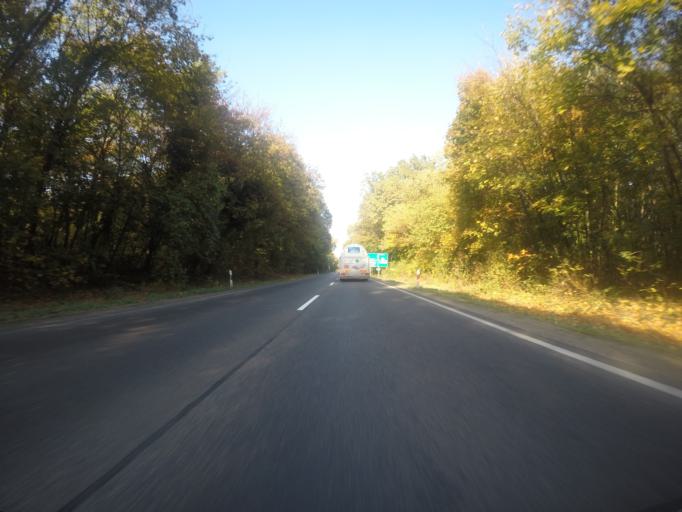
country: HU
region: Fejer
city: dunaujvaros
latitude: 46.9771
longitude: 18.9109
